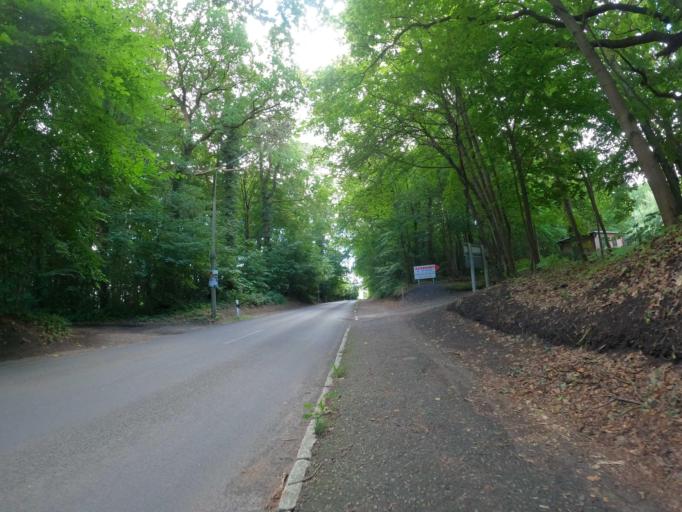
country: DE
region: Mecklenburg-Vorpommern
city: Putbus
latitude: 54.3574
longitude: 13.4760
